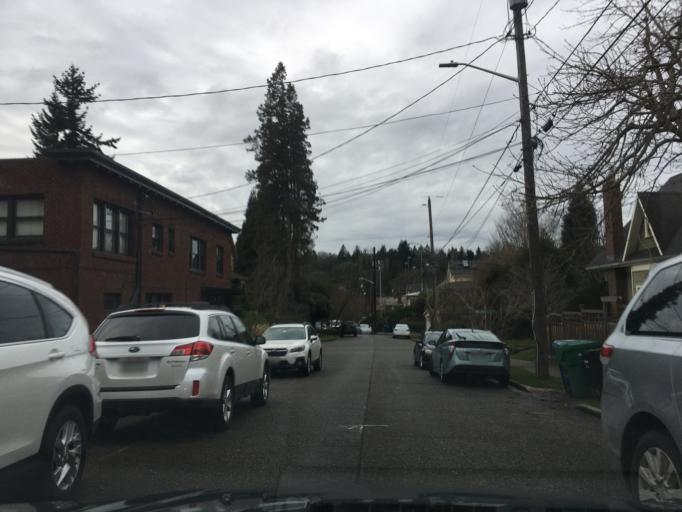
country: US
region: Washington
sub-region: King County
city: Seattle
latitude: 47.6665
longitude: -122.3379
